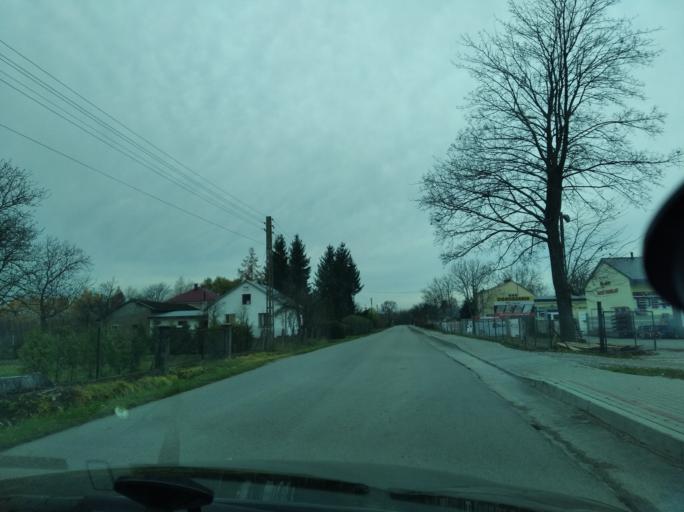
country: PL
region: Subcarpathian Voivodeship
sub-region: Powiat przeworski
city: Grzeska
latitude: 50.0835
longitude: 22.4519
